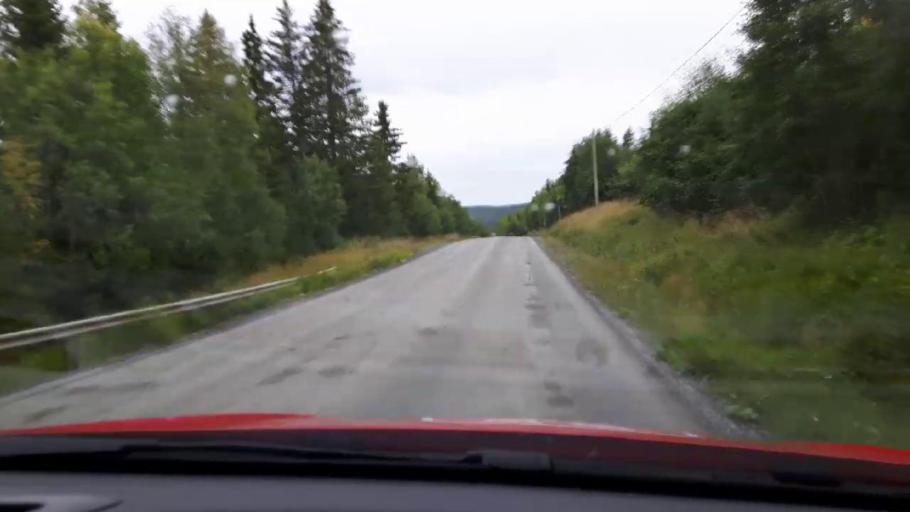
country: SE
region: Jaemtland
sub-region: Are Kommun
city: Jarpen
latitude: 63.4139
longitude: 13.3560
